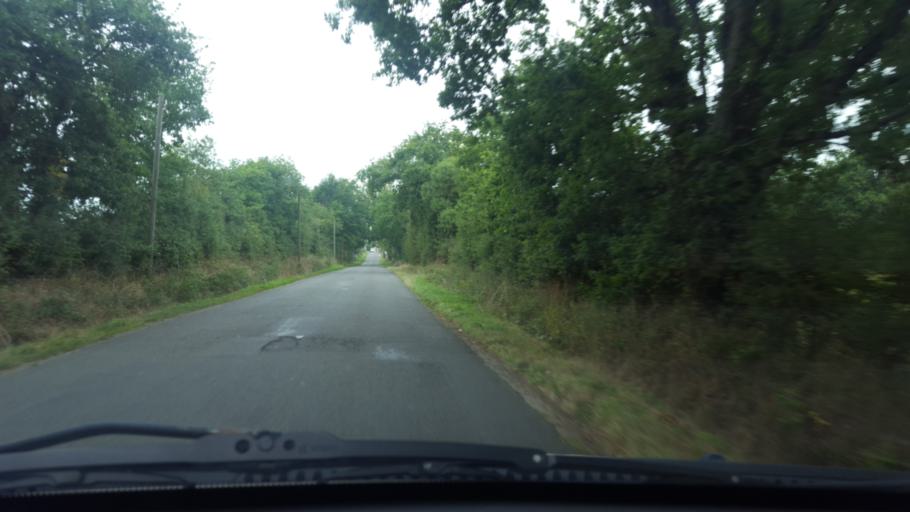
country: FR
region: Pays de la Loire
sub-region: Departement de la Loire-Atlantique
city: Saint-Philbert-de-Grand-Lieu
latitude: 46.9970
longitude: -1.6429
